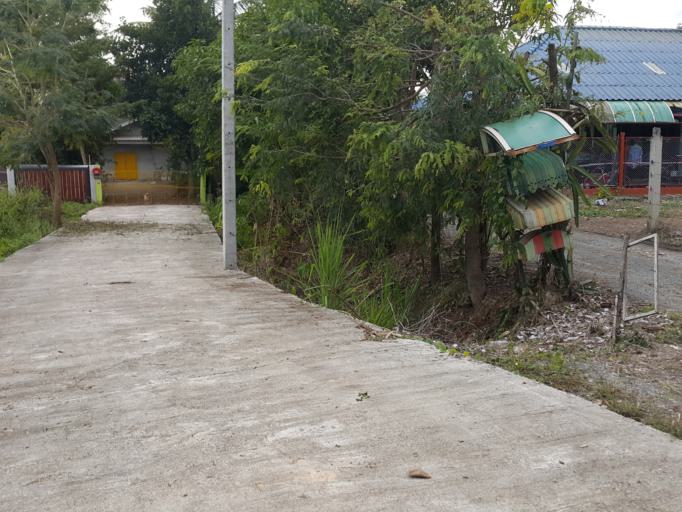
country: TH
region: Chiang Mai
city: San Sai
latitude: 18.8658
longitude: 99.1137
